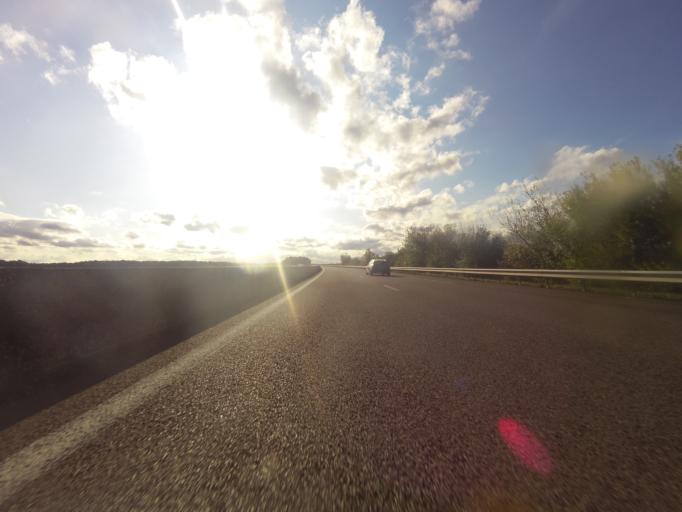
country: FR
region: Picardie
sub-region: Departement de la Somme
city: Quevauvillers
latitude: 49.8403
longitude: 2.0877
